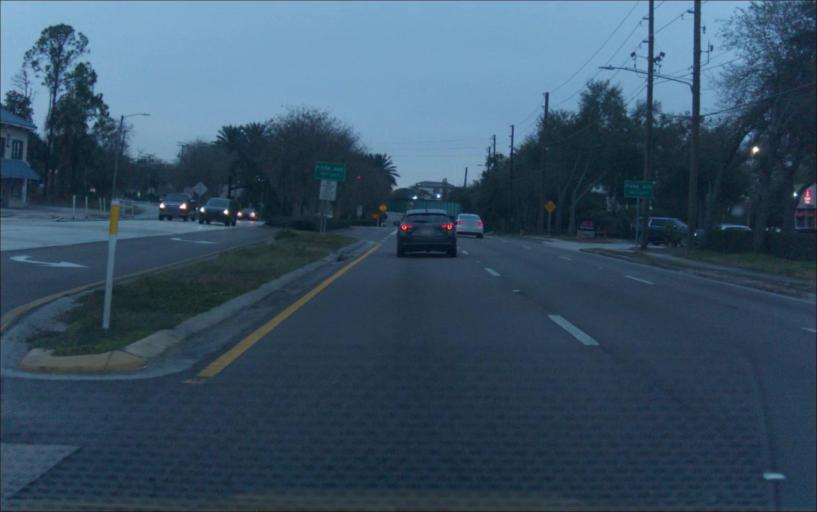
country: US
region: Florida
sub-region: Orange County
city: Eatonville
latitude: 28.6065
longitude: -81.3640
